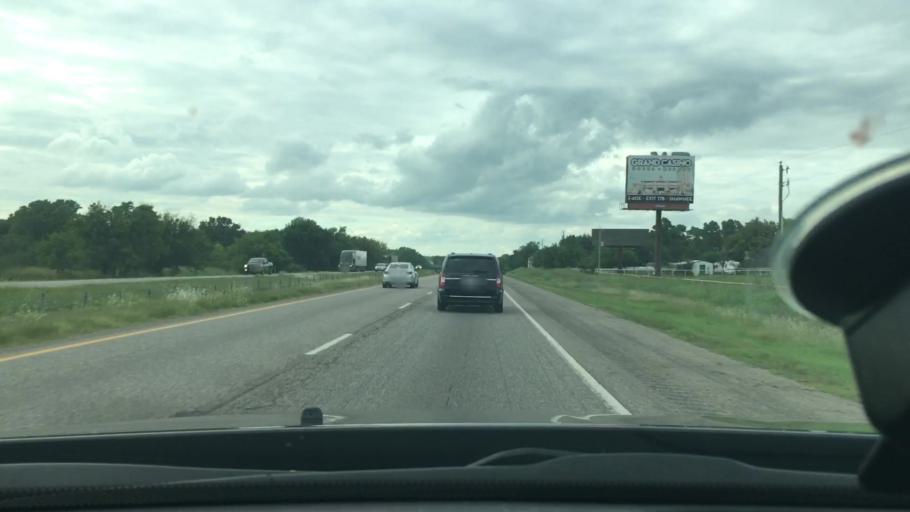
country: US
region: Oklahoma
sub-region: Cleveland County
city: Noble
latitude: 35.1076
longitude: -97.4343
